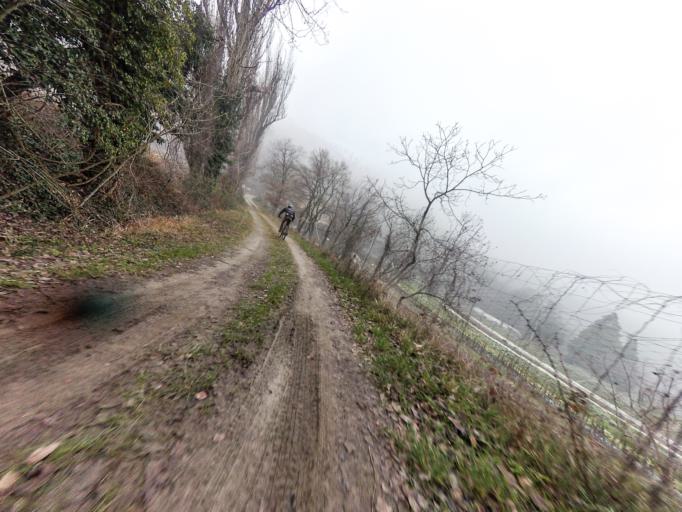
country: IT
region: Emilia-Romagna
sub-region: Provincia di Bologna
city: Monterenzio
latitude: 44.3261
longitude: 11.3474
